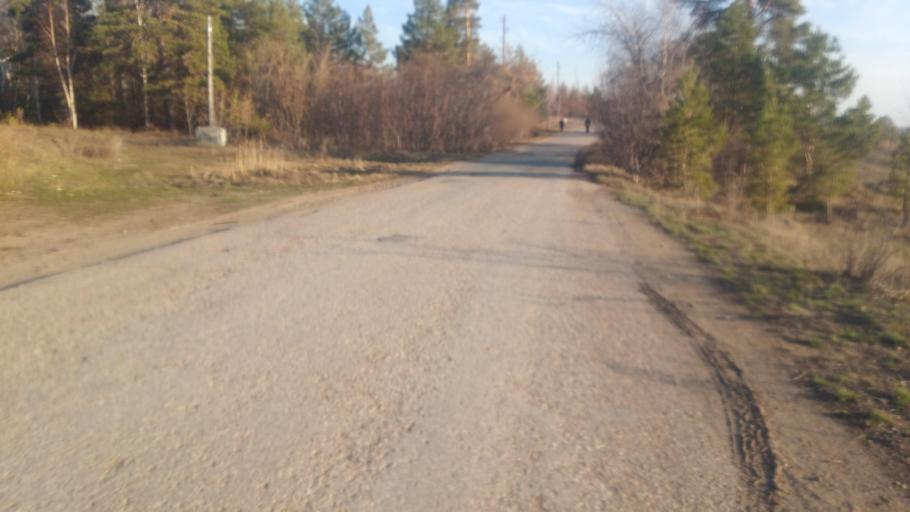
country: RU
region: Chelyabinsk
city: Novosineglazovskiy
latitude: 55.1263
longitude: 61.3286
